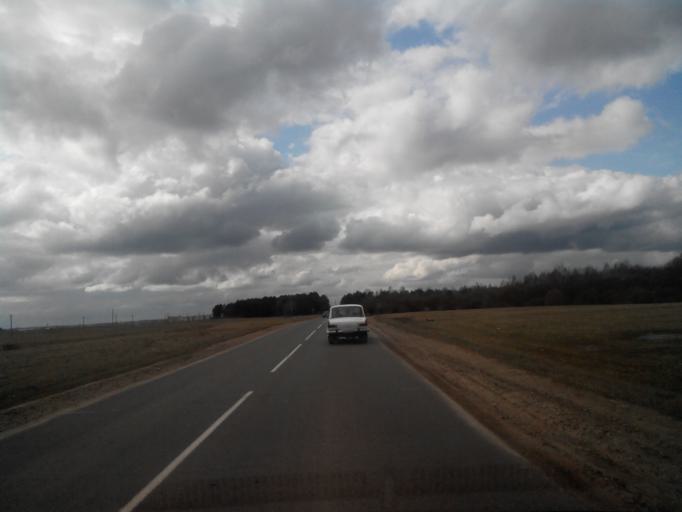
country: BY
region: Vitebsk
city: Pastavy
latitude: 55.1115
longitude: 26.8983
